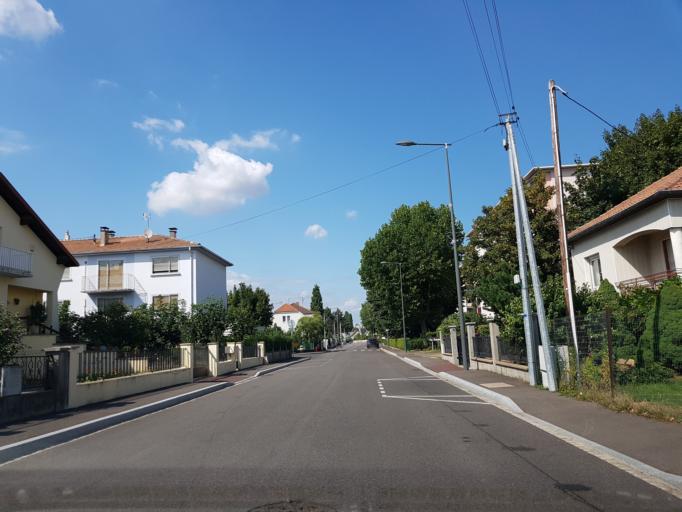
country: FR
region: Alsace
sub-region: Departement du Haut-Rhin
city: Illzach
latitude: 47.7807
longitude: 7.3530
